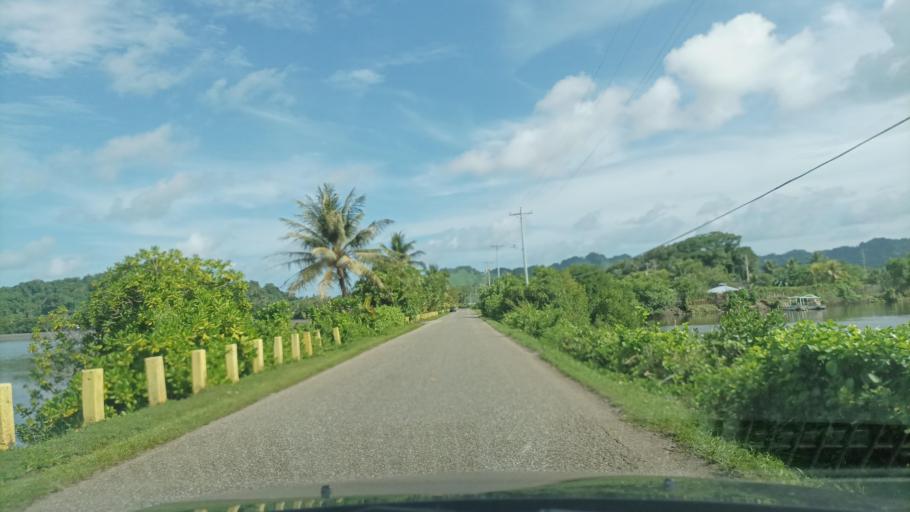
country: FM
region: Kosrae
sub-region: Lelu Municipality
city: Lelu
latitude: 5.3389
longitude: 163.0201
